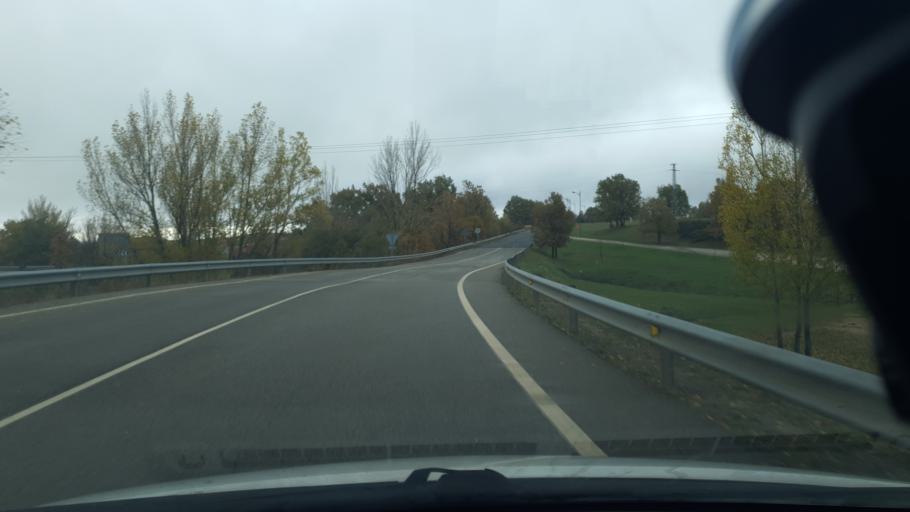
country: ES
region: Castille and Leon
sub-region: Provincia de Segovia
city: Riaza
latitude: 41.2714
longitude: -3.4944
